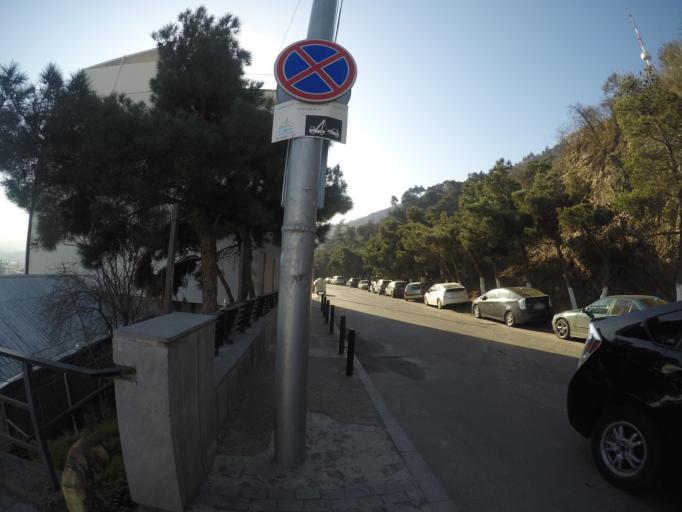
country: GE
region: T'bilisi
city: Tbilisi
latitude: 41.6982
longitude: 44.7909
